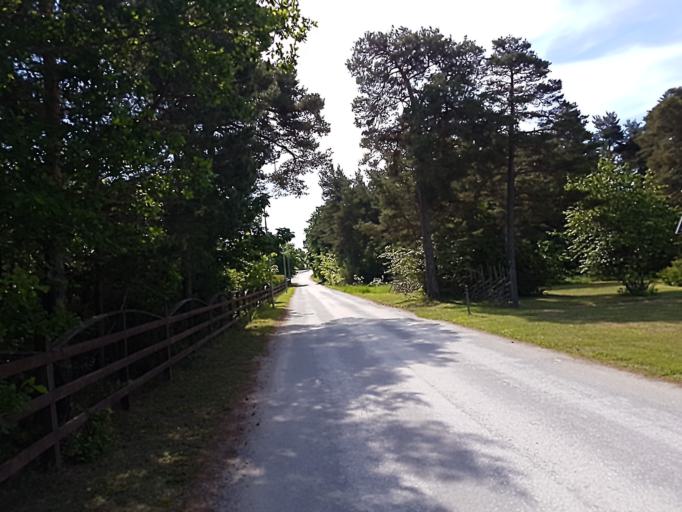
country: SE
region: Gotland
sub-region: Gotland
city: Visby
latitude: 57.8006
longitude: 18.5102
